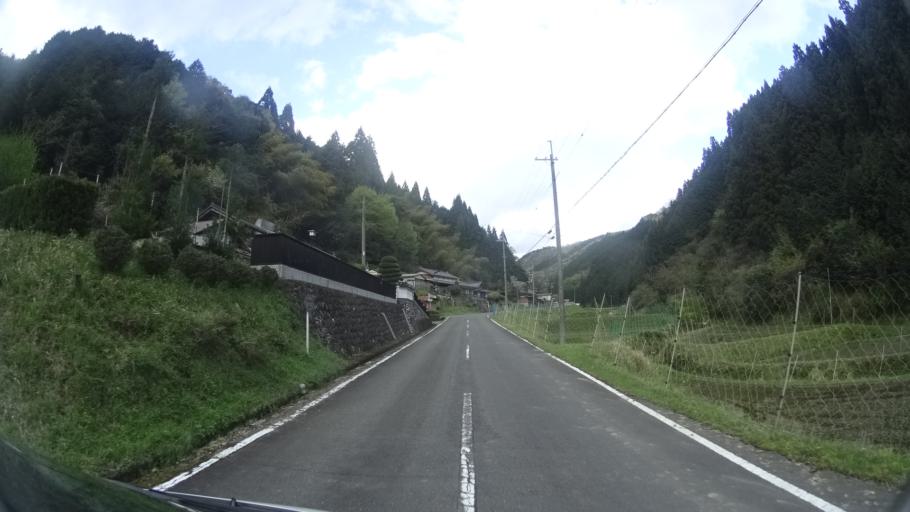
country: JP
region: Kyoto
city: Ayabe
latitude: 35.2496
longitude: 135.3039
